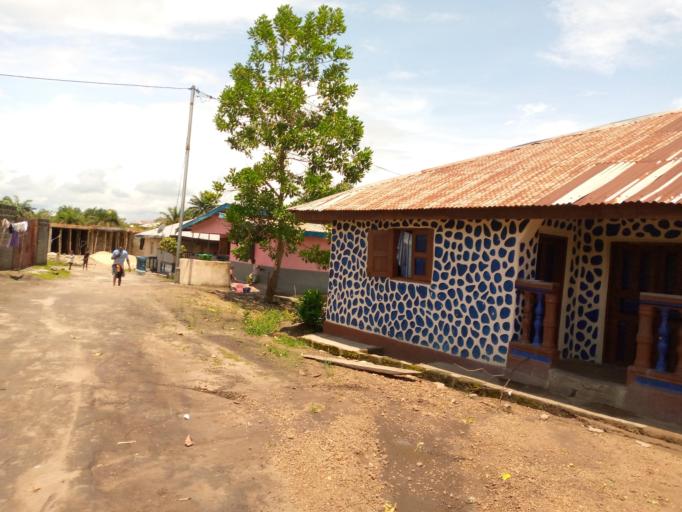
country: SL
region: Northern Province
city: Magburaka
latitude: 8.7227
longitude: -11.9269
